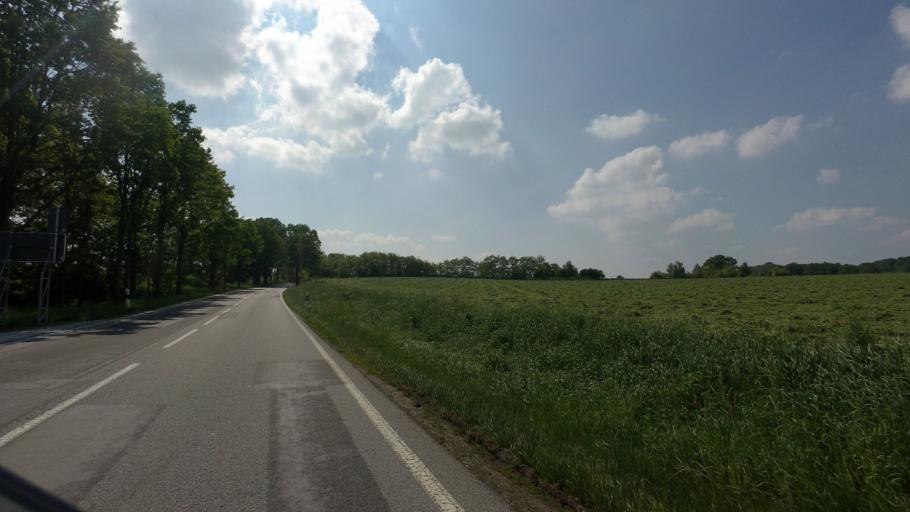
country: DE
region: Saxony
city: Weissenberg
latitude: 51.1879
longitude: 14.6755
